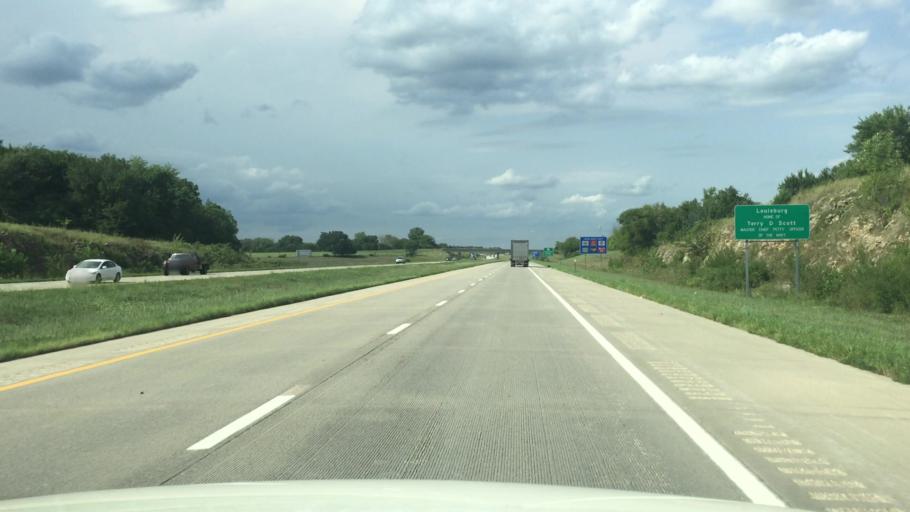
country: US
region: Kansas
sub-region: Miami County
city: Louisburg
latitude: 38.6076
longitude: -94.6941
